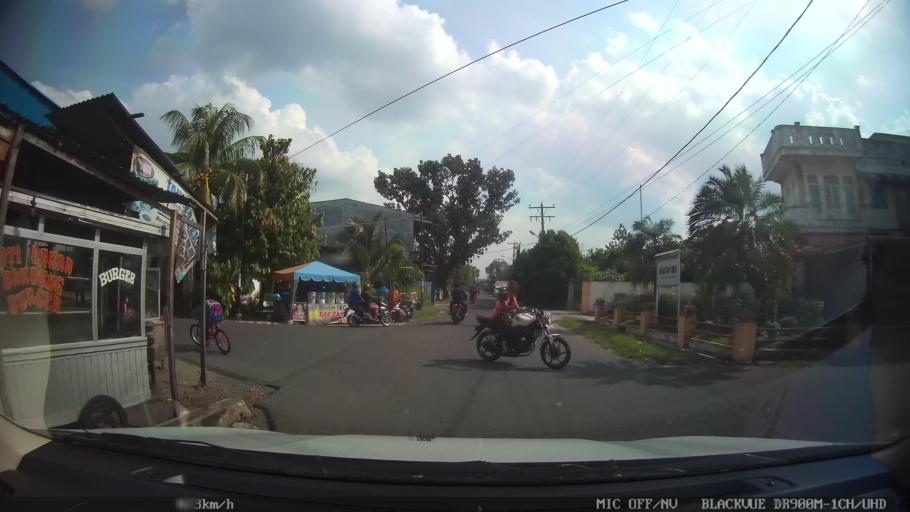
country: ID
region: North Sumatra
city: Binjai
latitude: 3.6133
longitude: 98.4988
